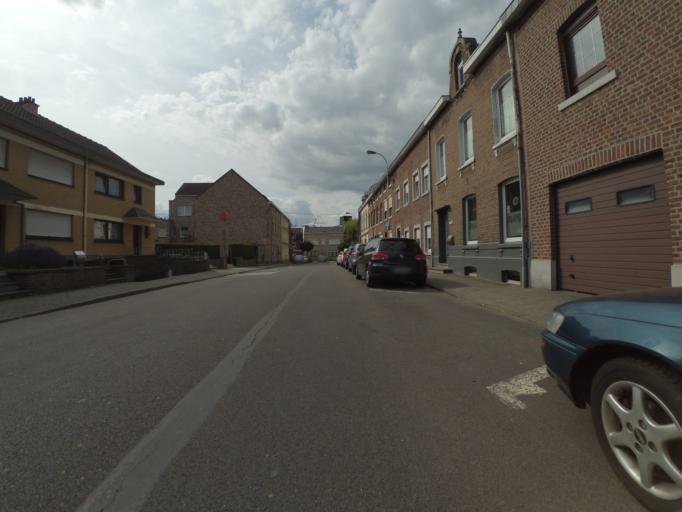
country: BE
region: Wallonia
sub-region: Province de Liege
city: La Calamine
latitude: 50.7185
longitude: 6.0104
